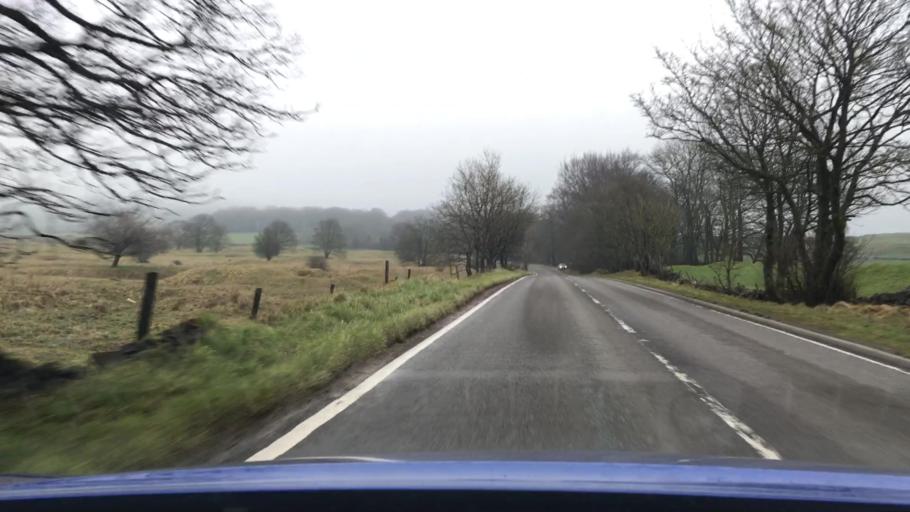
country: GB
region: England
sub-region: Derbyshire
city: High Peak
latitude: 53.3171
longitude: -1.8485
